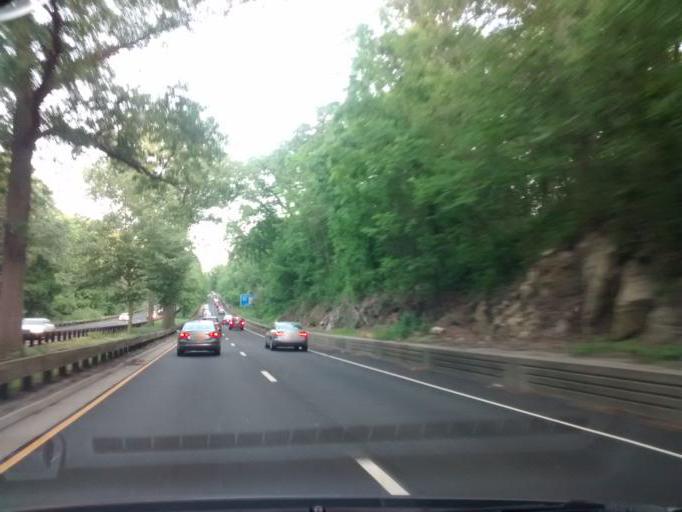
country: US
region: Connecticut
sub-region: Fairfield County
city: Glenville
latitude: 41.0528
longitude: -73.6734
